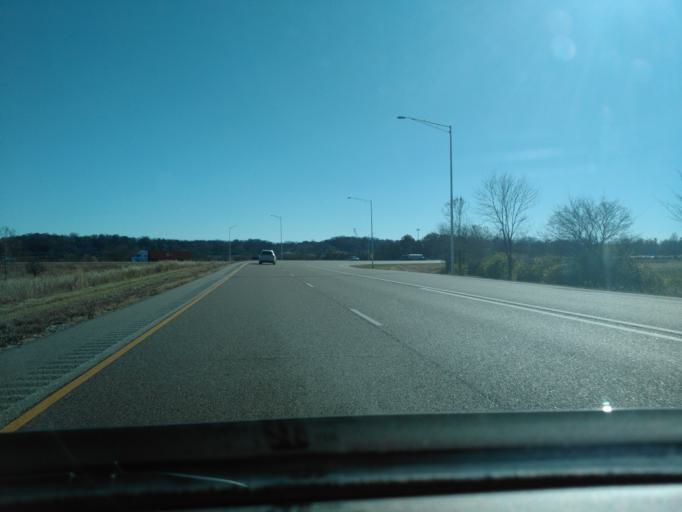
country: US
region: Illinois
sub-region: Saint Clair County
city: Caseyville
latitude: 38.6695
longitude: -90.0314
